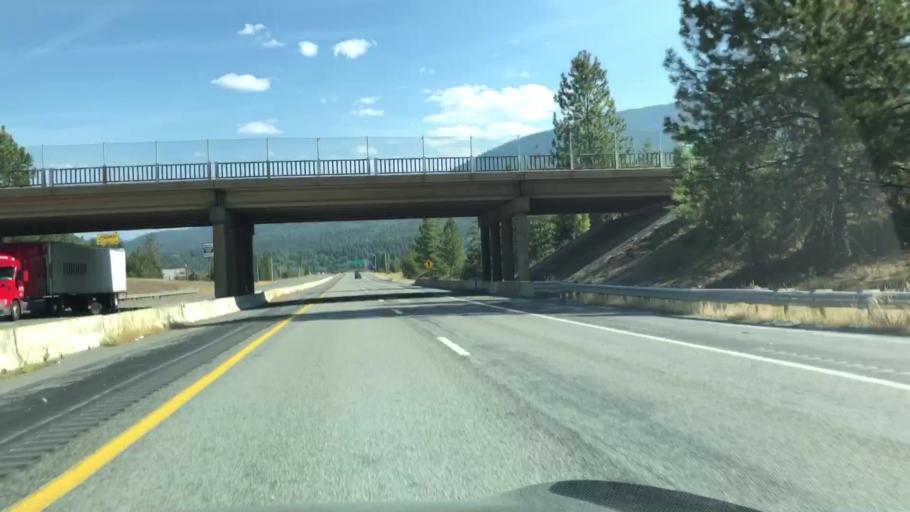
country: US
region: Idaho
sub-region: Shoshone County
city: Kellogg
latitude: 47.5460
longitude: -116.1334
